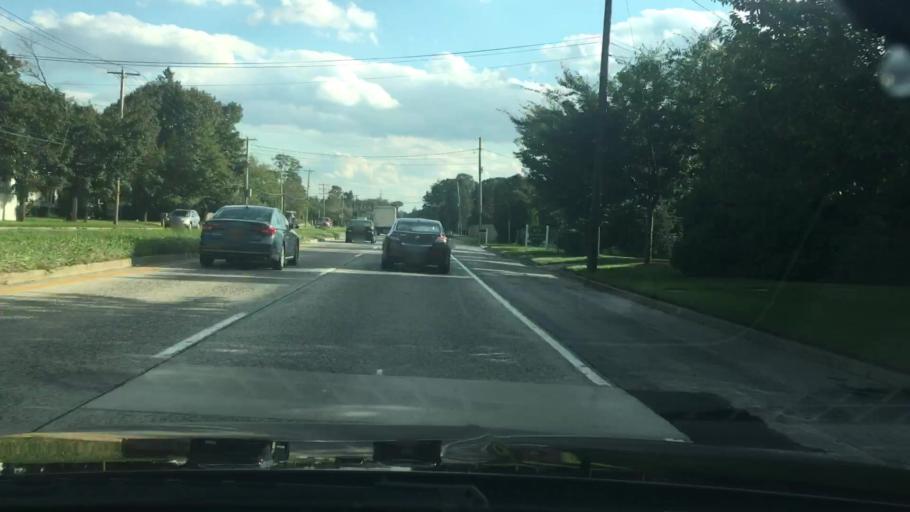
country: US
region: New York
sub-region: Suffolk County
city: Dix Hills
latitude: 40.7874
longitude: -73.3401
